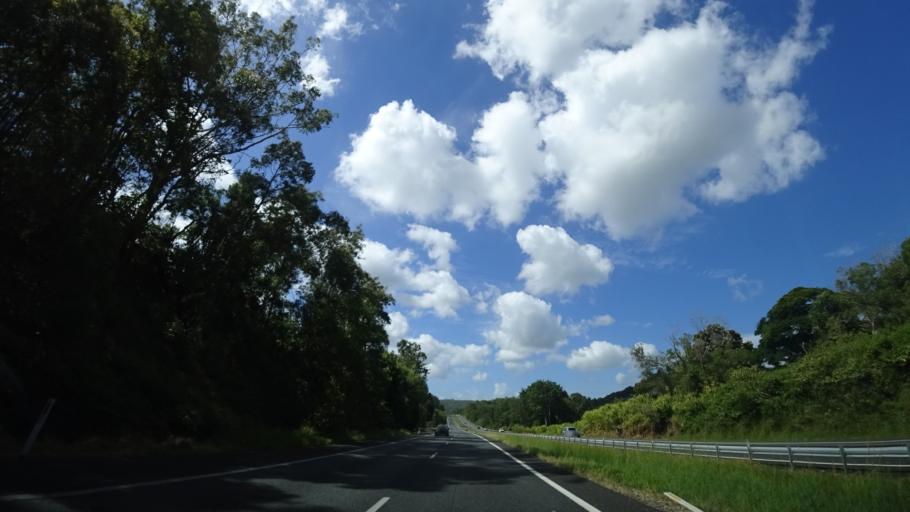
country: AU
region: Queensland
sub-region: Sunshine Coast
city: Twin Waters
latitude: -26.6336
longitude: 152.9877
